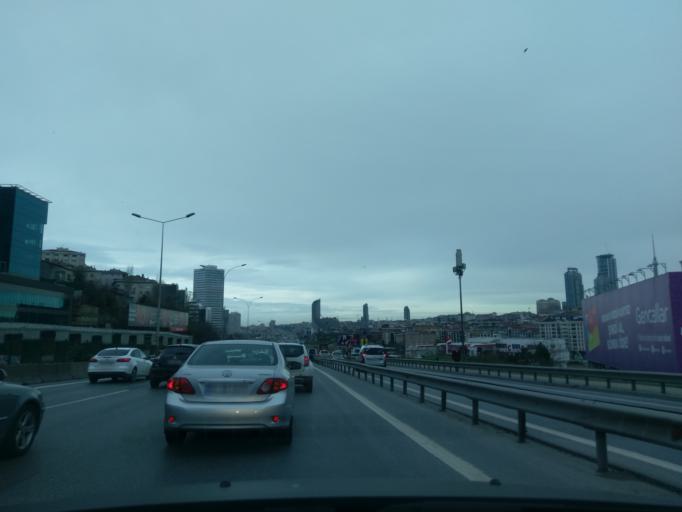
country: TR
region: Istanbul
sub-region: Atasehir
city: Atasehir
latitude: 40.9887
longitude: 29.0837
